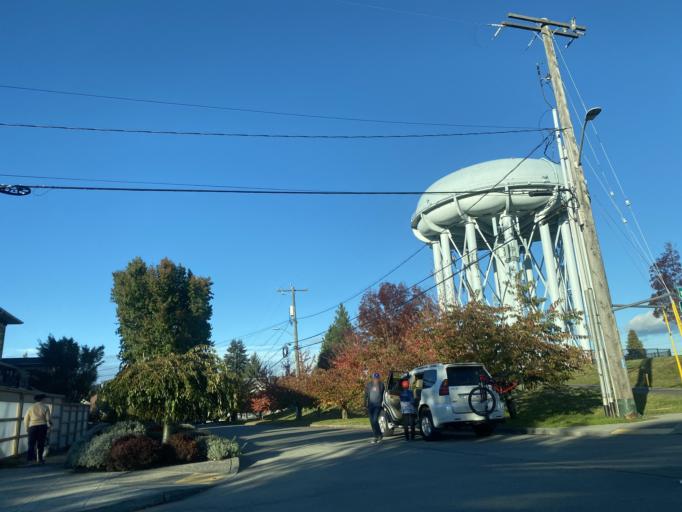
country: US
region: Washington
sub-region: King County
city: Seattle
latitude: 47.6486
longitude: -122.4070
